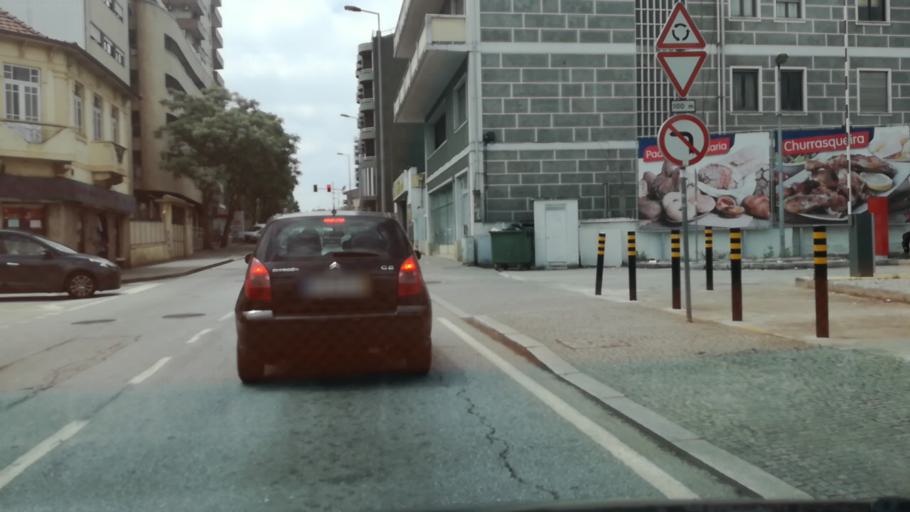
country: PT
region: Porto
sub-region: Trofa
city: Bougado
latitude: 41.3387
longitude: -8.5591
